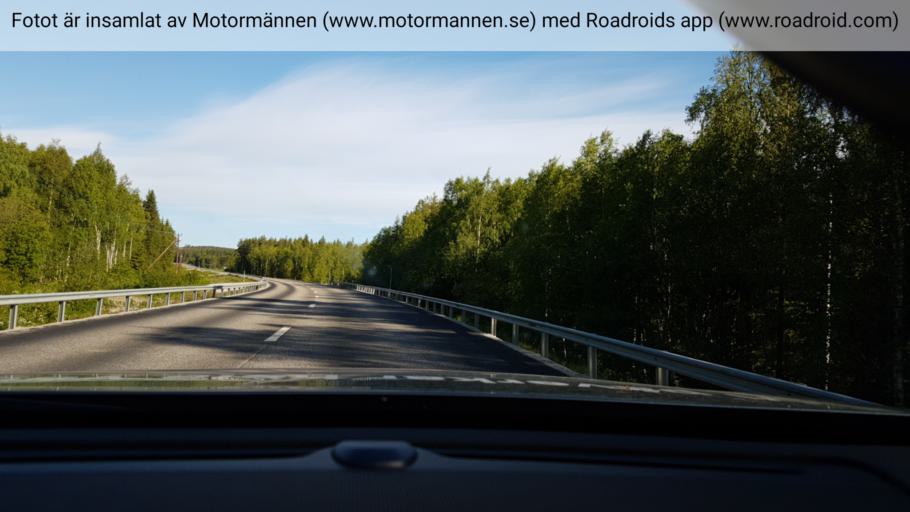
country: SE
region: Vaesterbotten
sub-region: Vannas Kommun
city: Vaennaes
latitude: 64.0441
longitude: 19.6869
